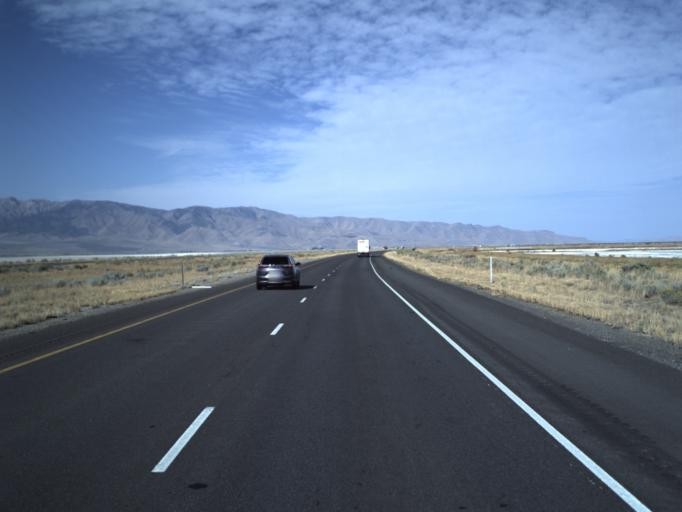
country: US
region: Utah
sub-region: Tooele County
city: Stansbury park
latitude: 40.6627
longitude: -112.3446
